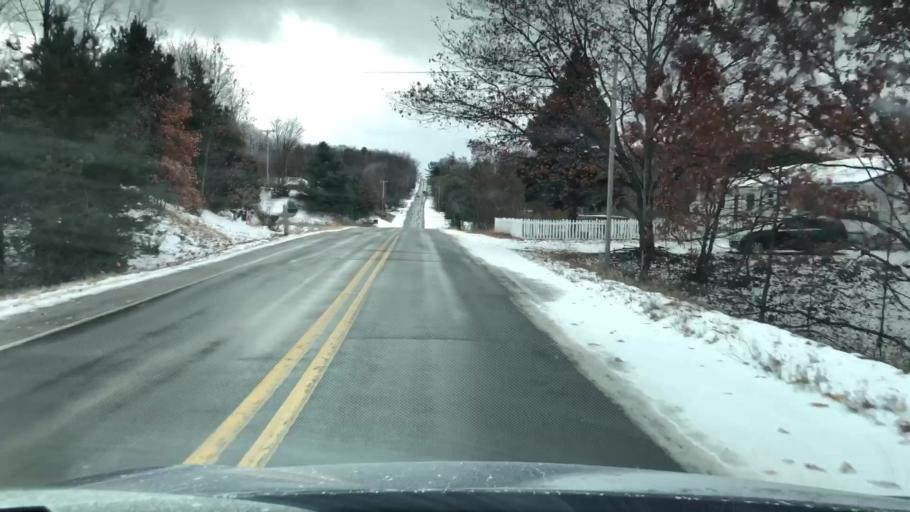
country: US
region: Michigan
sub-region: Antrim County
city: Elk Rapids
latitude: 44.8941
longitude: -85.5155
